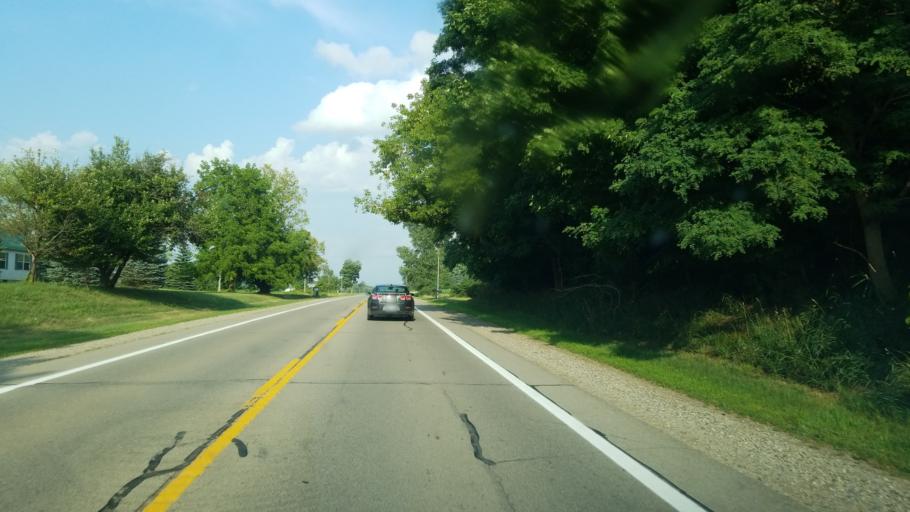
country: US
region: Michigan
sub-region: Gratiot County
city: Alma
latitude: 43.4083
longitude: -84.7223
